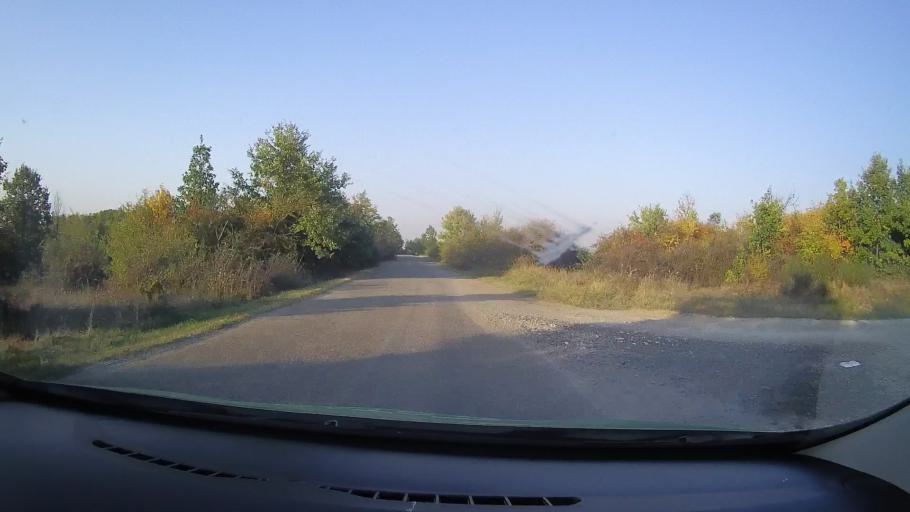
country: RO
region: Arad
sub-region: Comuna Silindia
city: Silindia
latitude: 46.3320
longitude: 21.9806
